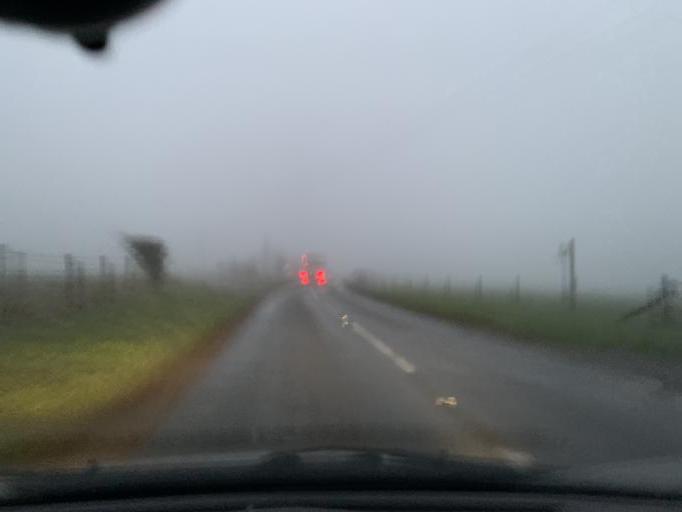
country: GB
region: England
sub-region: Wiltshire
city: Shrewton
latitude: 51.2016
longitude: -1.8784
